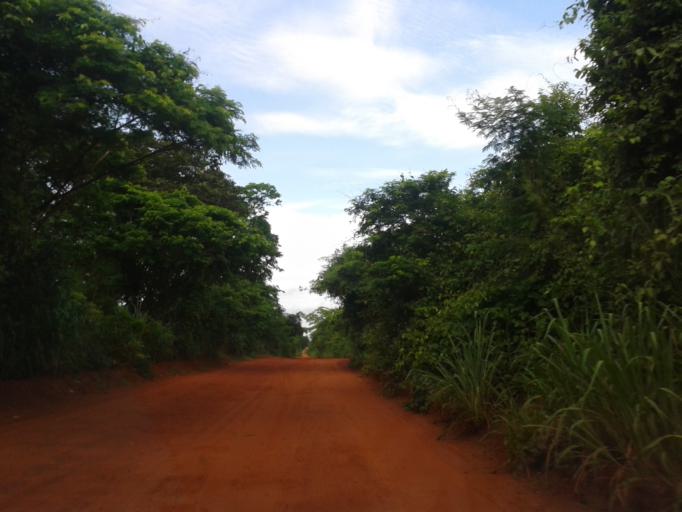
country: BR
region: Minas Gerais
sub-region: Santa Vitoria
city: Santa Vitoria
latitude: -19.1186
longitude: -50.5332
